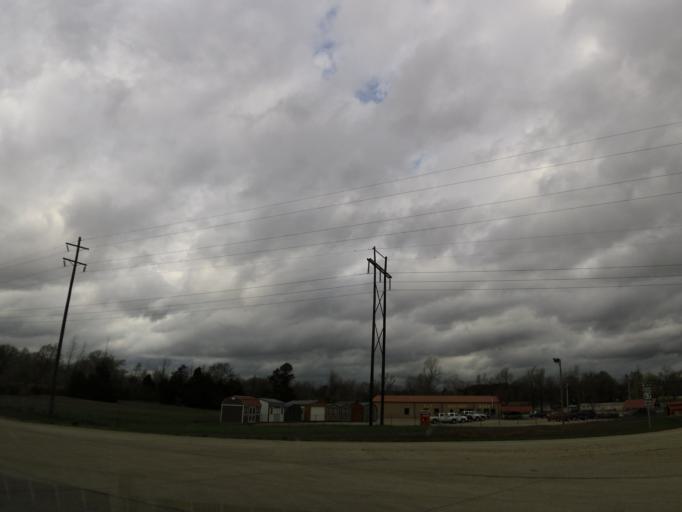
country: US
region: Missouri
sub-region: Butler County
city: Poplar Bluff
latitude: 36.7293
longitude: -90.4634
